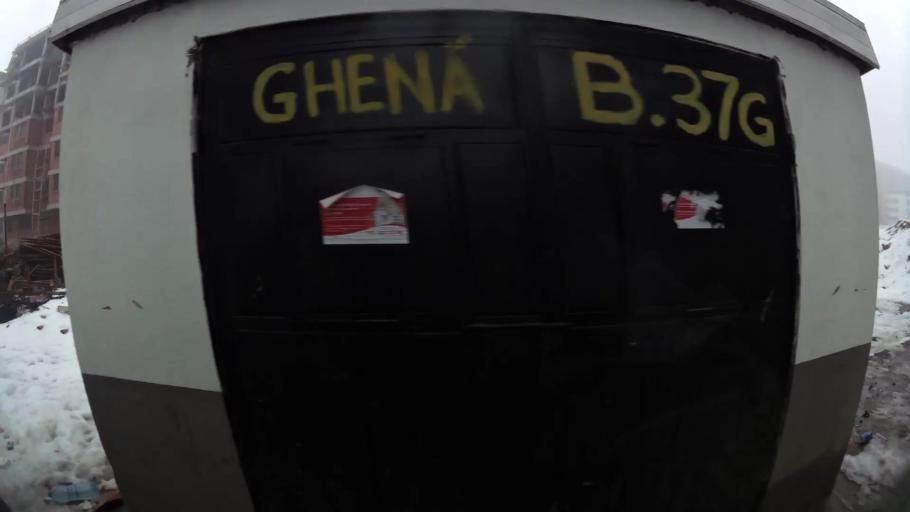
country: RO
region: Ilfov
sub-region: Comuna Chiajna
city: Chiajna
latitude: 44.4462
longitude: 25.9783
